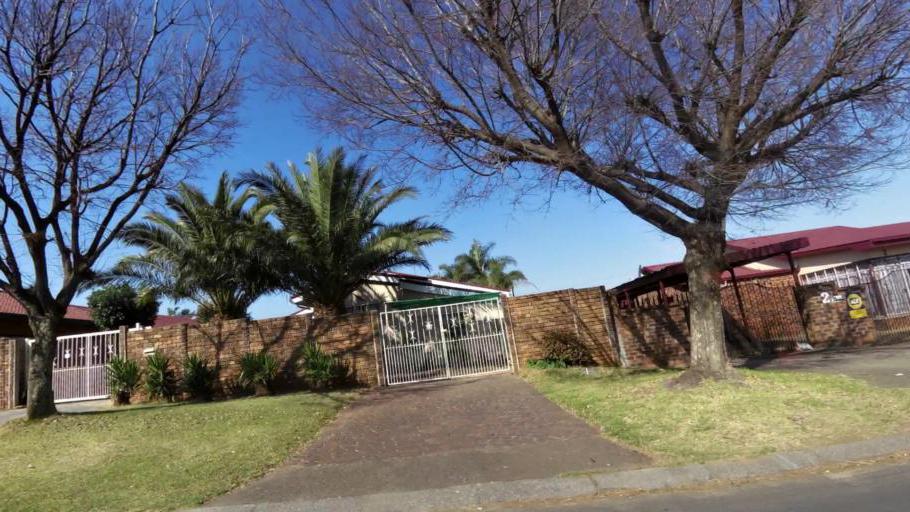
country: ZA
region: Gauteng
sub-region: City of Johannesburg Metropolitan Municipality
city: Johannesburg
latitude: -26.1752
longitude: 27.9709
